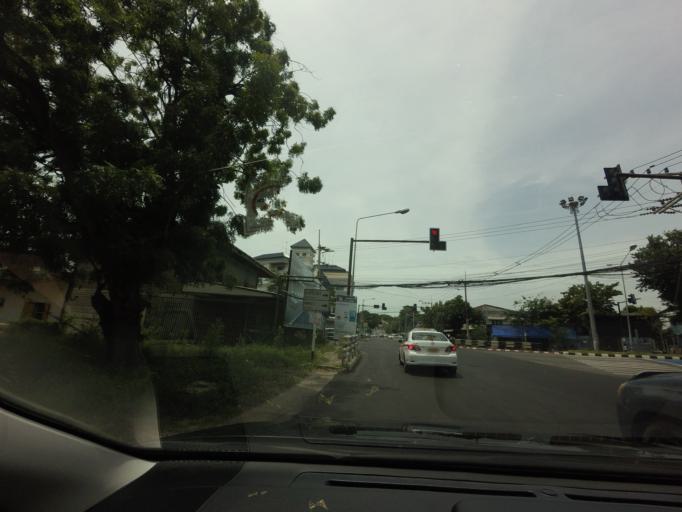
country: TH
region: Chon Buri
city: Chon Buri
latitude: 13.3023
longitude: 100.9030
